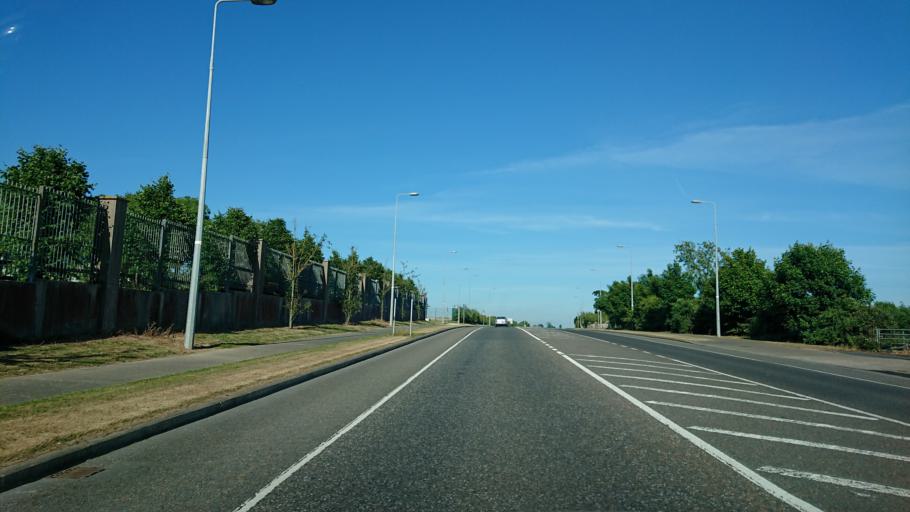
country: IE
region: Munster
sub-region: Waterford
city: Waterford
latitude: 52.2523
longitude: -7.1612
